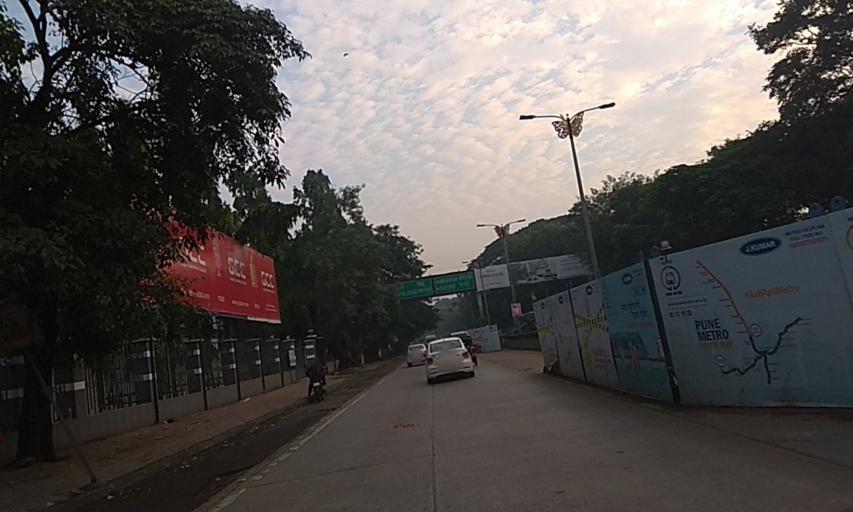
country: IN
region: Maharashtra
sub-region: Pune Division
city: Shivaji Nagar
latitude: 18.5380
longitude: 73.8817
